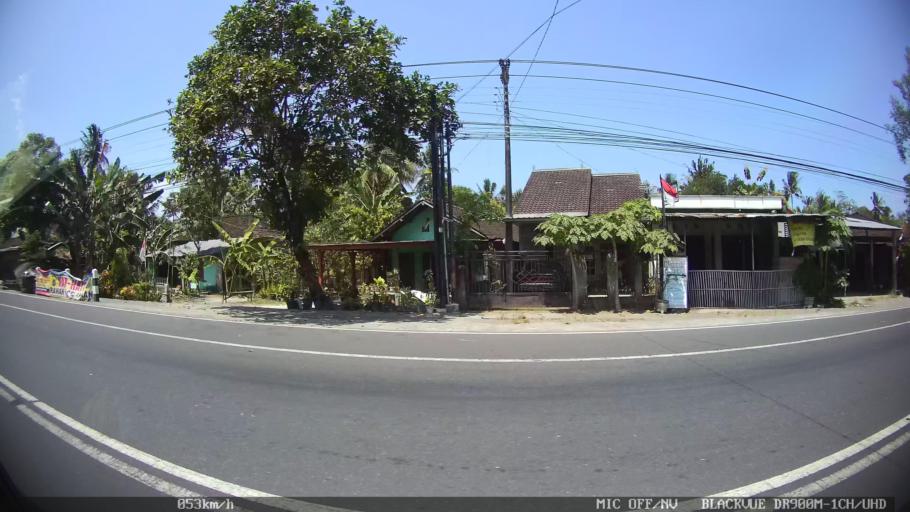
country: ID
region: Daerah Istimewa Yogyakarta
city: Srandakan
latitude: -7.9383
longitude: 110.2558
